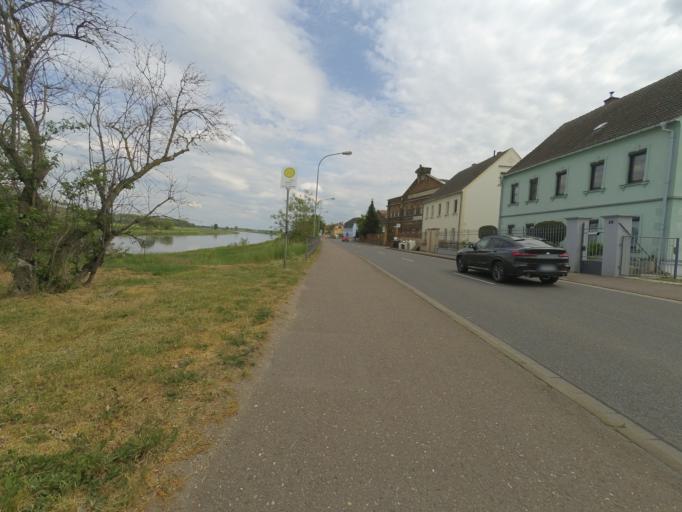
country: DE
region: Saxony
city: Strehla
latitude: 51.3495
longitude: 13.2425
